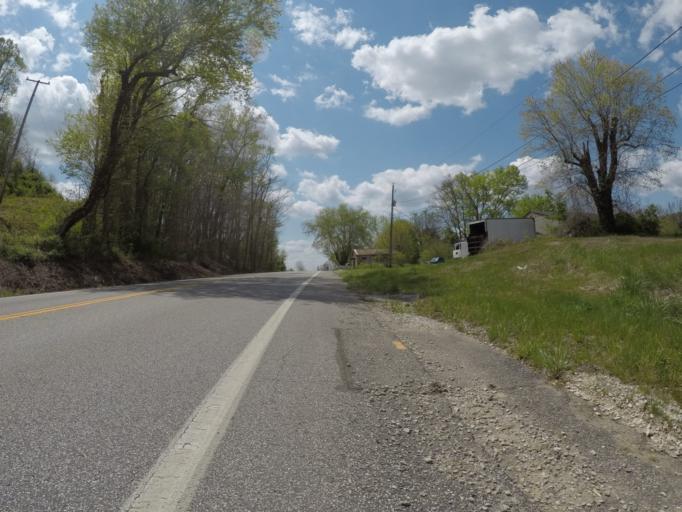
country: US
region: West Virginia
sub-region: Cabell County
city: Pea Ridge
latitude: 38.4516
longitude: -82.3757
